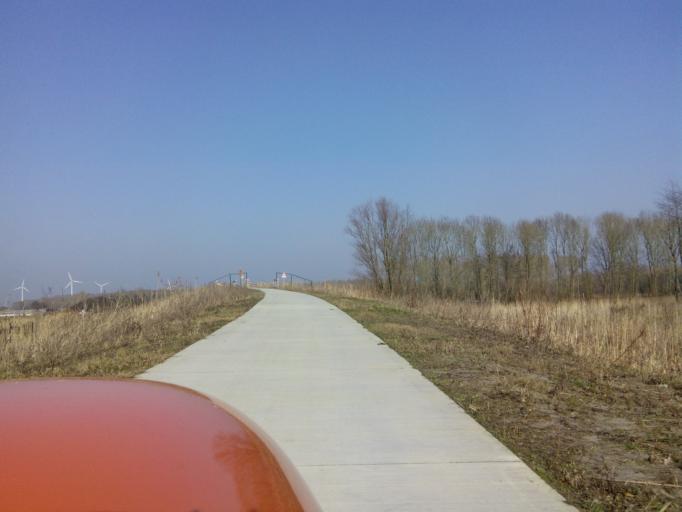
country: NL
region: Flevoland
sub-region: Gemeente Zeewolde
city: Zeewolde
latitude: 52.3238
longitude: 5.4487
